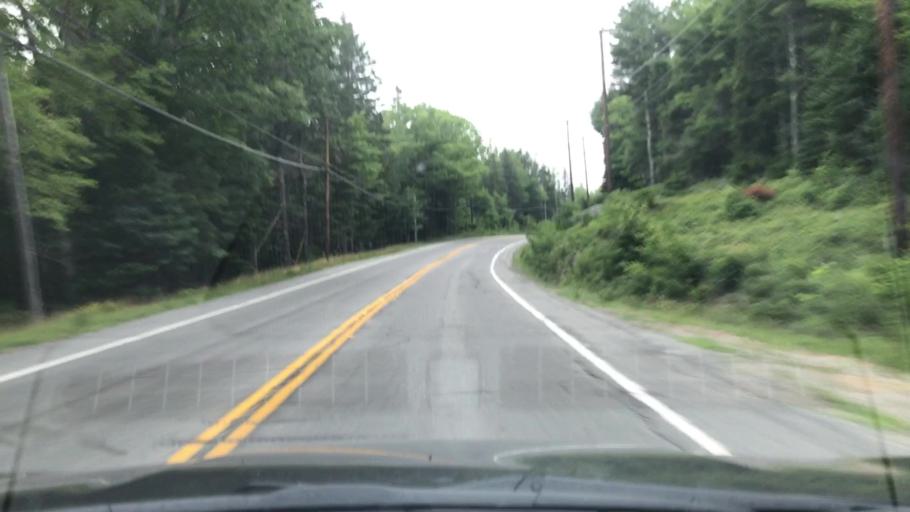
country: US
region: Maine
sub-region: Hancock County
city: Trenton
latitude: 44.3826
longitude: -68.3313
